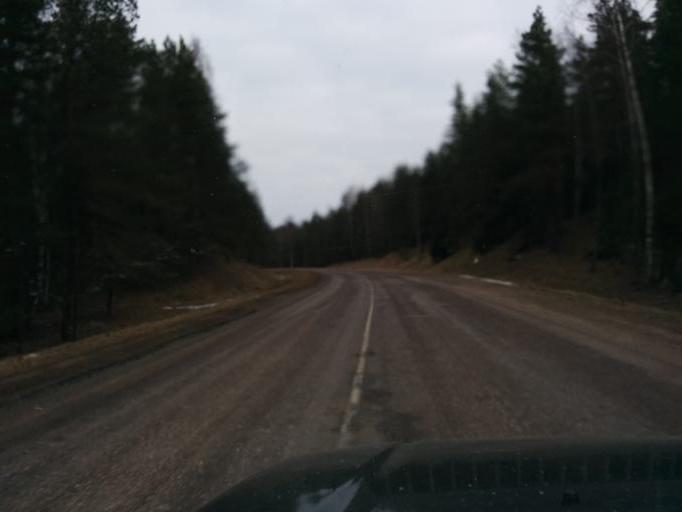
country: LV
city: Tireli
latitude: 56.8874
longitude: 23.5380
